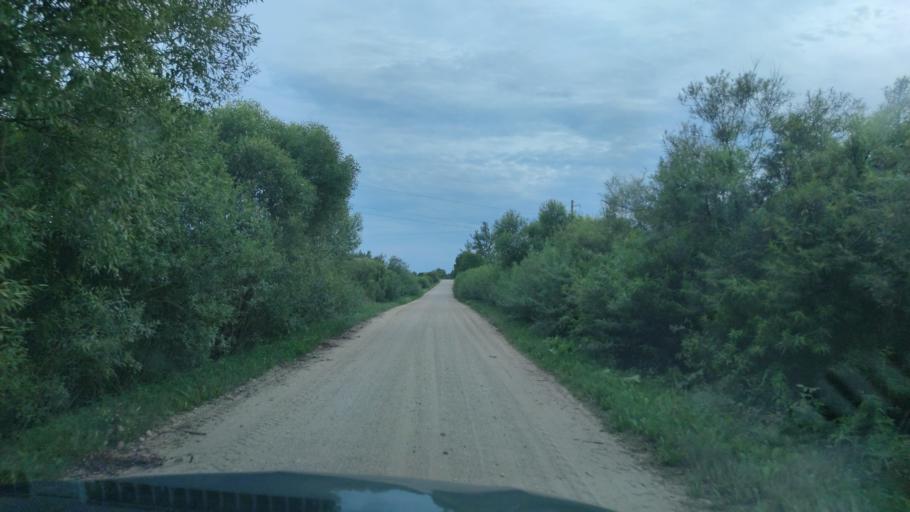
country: BY
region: Vitebsk
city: Mosar
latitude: 55.1271
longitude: 27.1586
